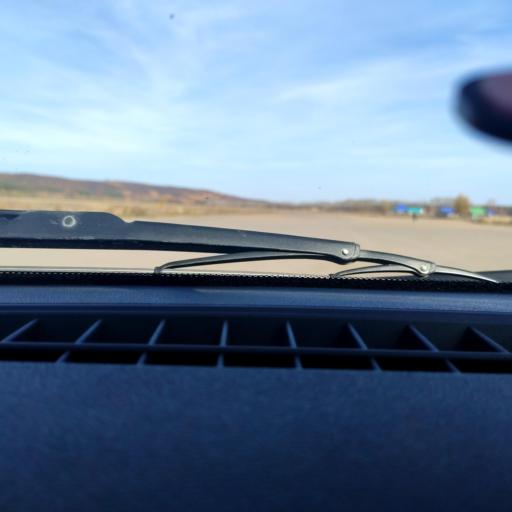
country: RU
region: Bashkortostan
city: Ufa
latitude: 54.8359
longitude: 56.1711
